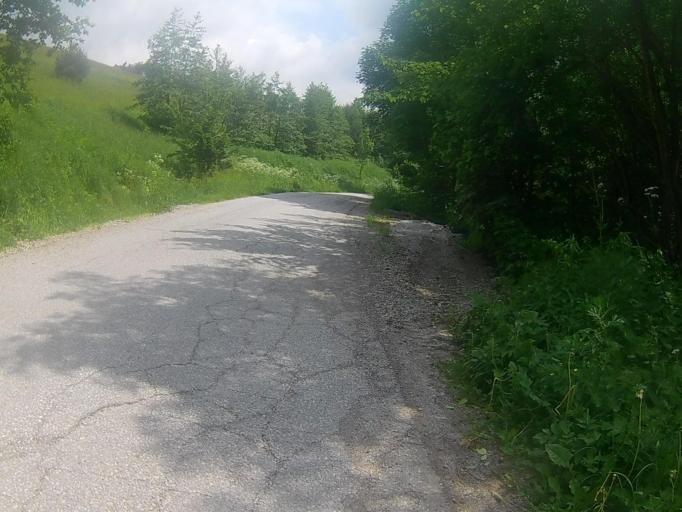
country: SI
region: Kungota
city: Zgornja Kungota
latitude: 46.6181
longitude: 15.5790
